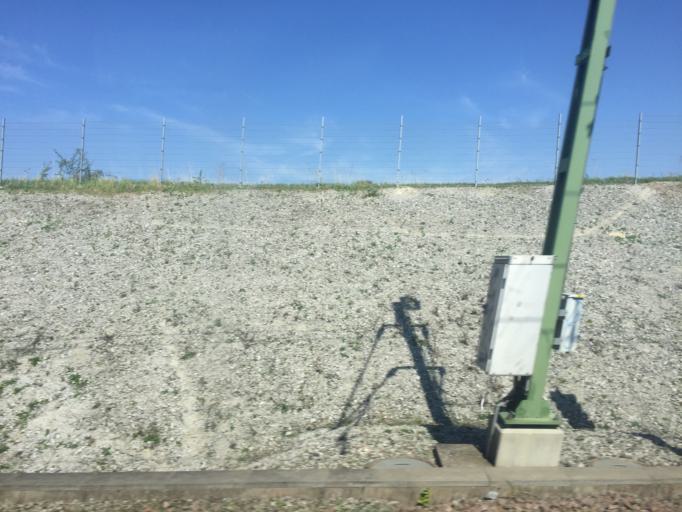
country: SE
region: Skane
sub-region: Malmo
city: Bunkeflostrand
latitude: 55.5606
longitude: 12.9393
